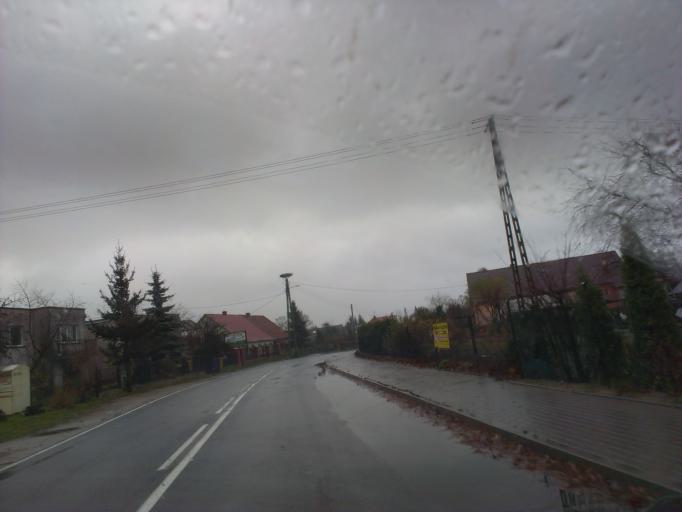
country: PL
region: West Pomeranian Voivodeship
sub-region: Powiat szczecinecki
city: Szczecinek
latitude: 53.6517
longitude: 16.6290
